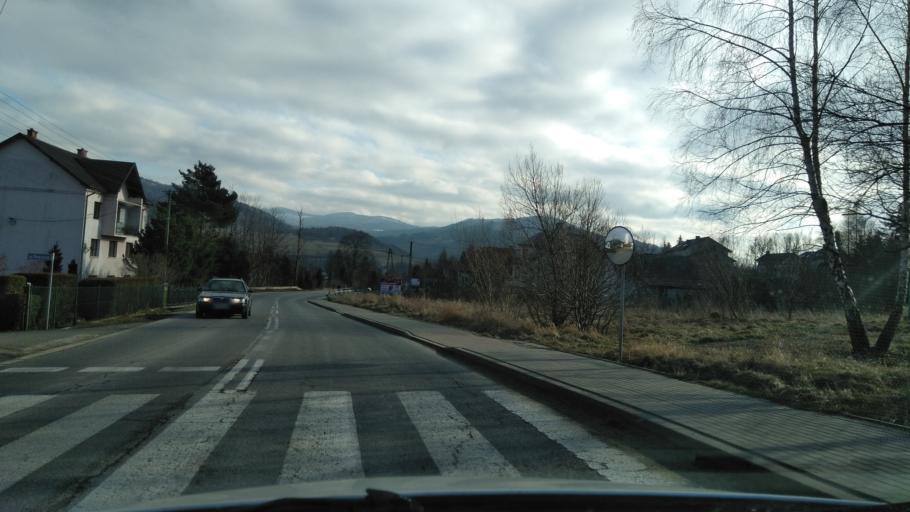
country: PL
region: Silesian Voivodeship
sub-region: Powiat zywiecki
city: Milowka
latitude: 49.5633
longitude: 19.0760
